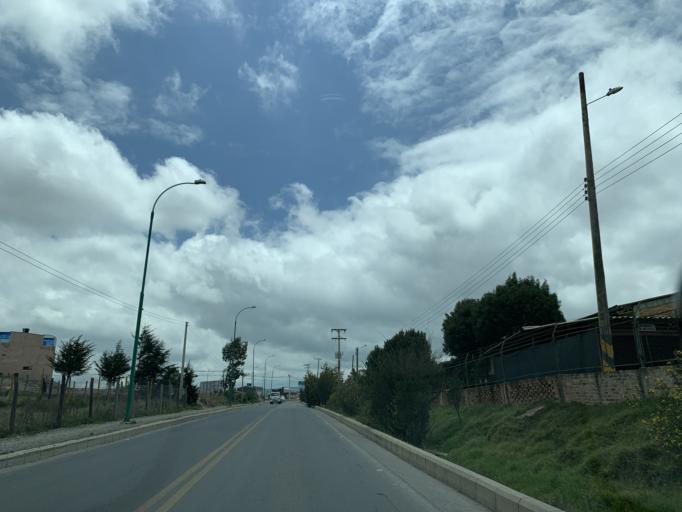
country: CO
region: Boyaca
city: Tunja
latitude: 5.5332
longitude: -73.3444
